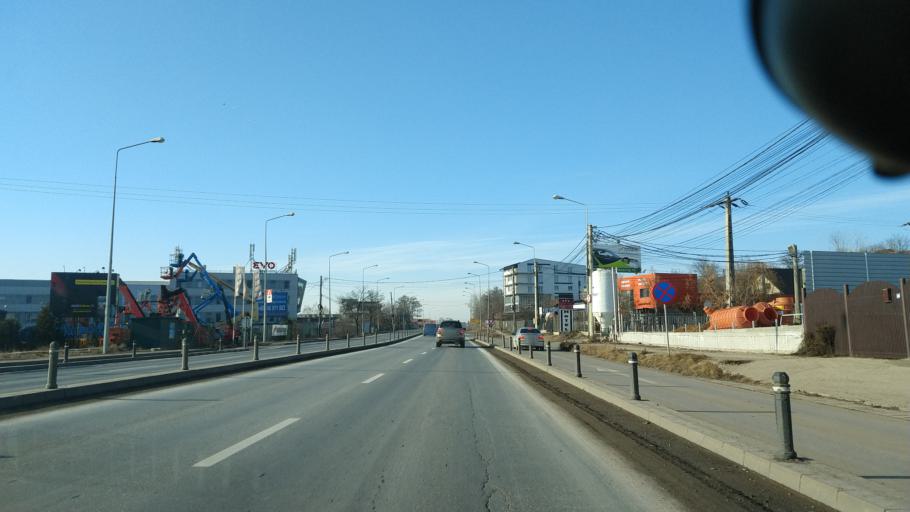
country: RO
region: Iasi
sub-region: Comuna Valea Lupului
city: Valea Lupului
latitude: 47.1732
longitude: 27.5115
